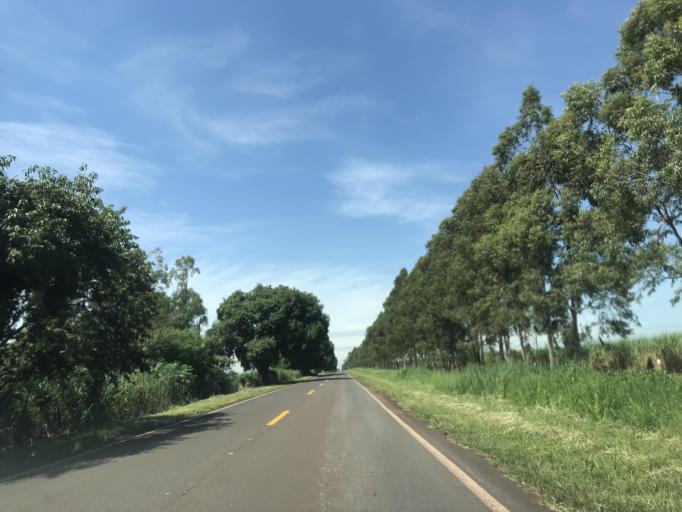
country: BR
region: Parana
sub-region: Paranavai
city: Nova Aurora
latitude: -22.8446
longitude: -52.6572
